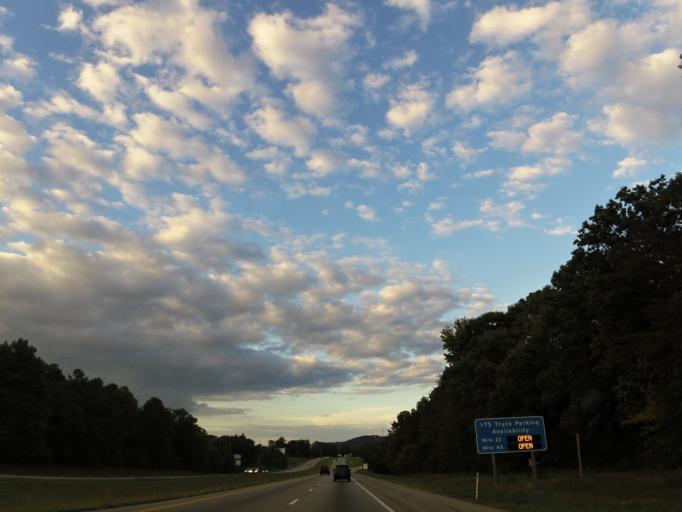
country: US
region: Tennessee
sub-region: Bradley County
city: Cleveland
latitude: 35.1797
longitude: -84.9126
